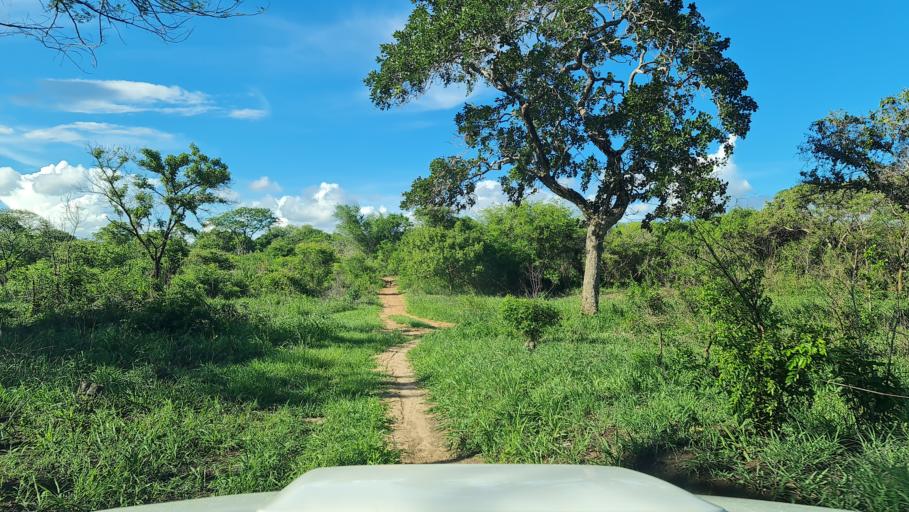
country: MZ
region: Nampula
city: Ilha de Mocambique
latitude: -15.2553
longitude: 40.1825
